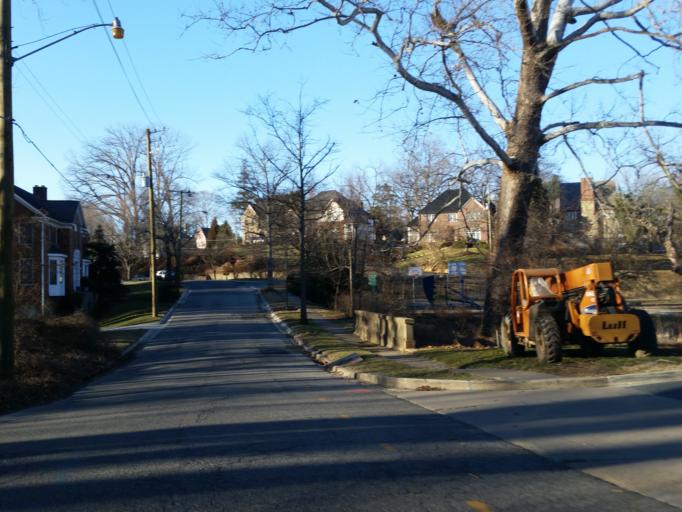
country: US
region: Maryland
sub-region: Montgomery County
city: Silver Spring
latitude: 38.9849
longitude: -77.0398
